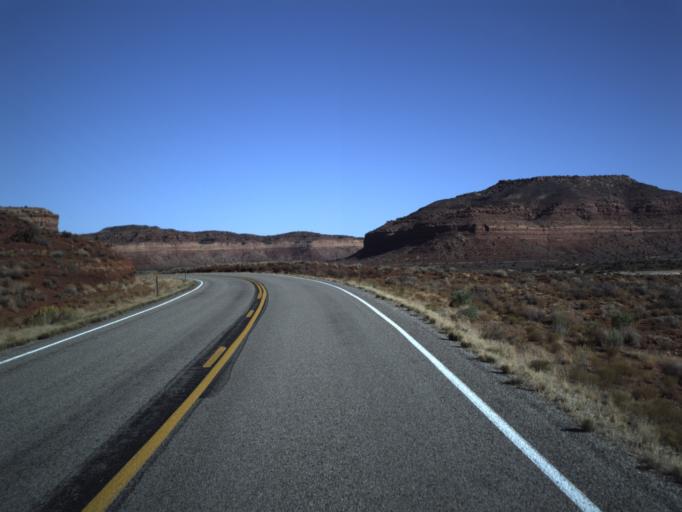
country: US
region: Utah
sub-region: San Juan County
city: Blanding
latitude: 37.7191
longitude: -110.2464
